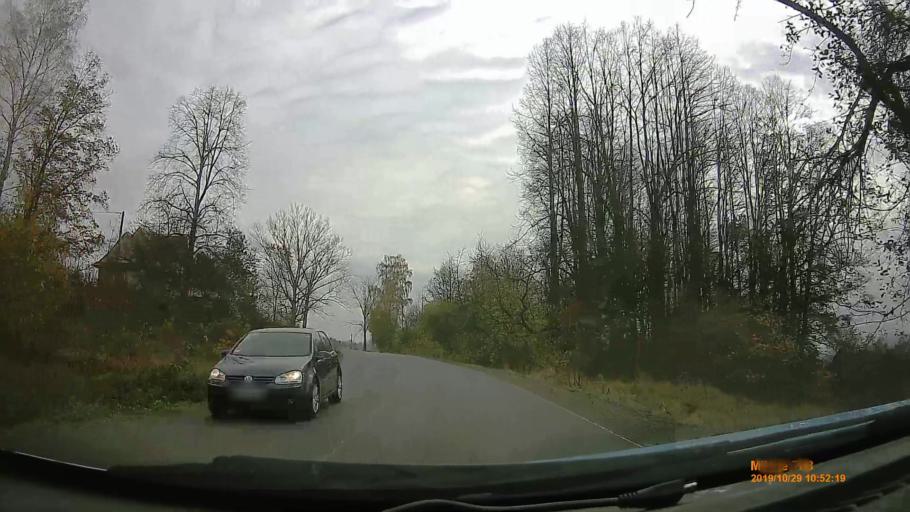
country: PL
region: Lower Silesian Voivodeship
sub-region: Powiat klodzki
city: Nowa Ruda
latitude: 50.5390
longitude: 16.4715
